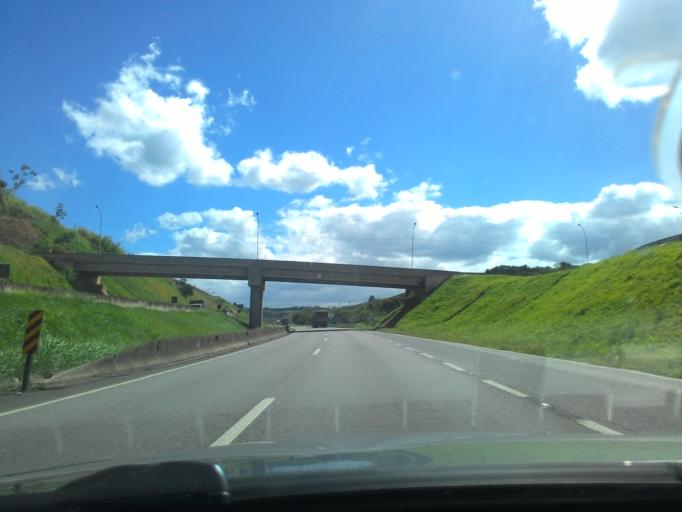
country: BR
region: Sao Paulo
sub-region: Cajati
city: Cajati
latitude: -24.7372
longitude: -48.1212
